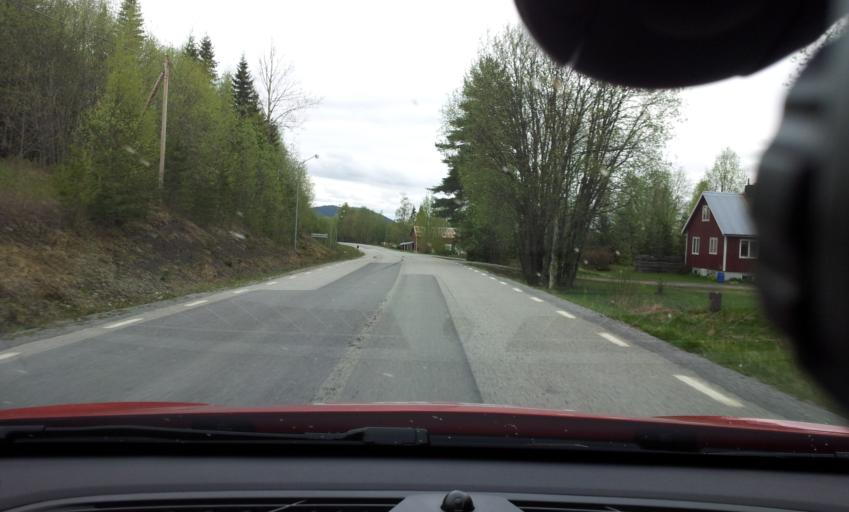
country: SE
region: Jaemtland
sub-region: Bergs Kommun
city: Hoverberg
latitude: 62.7793
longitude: 14.5142
